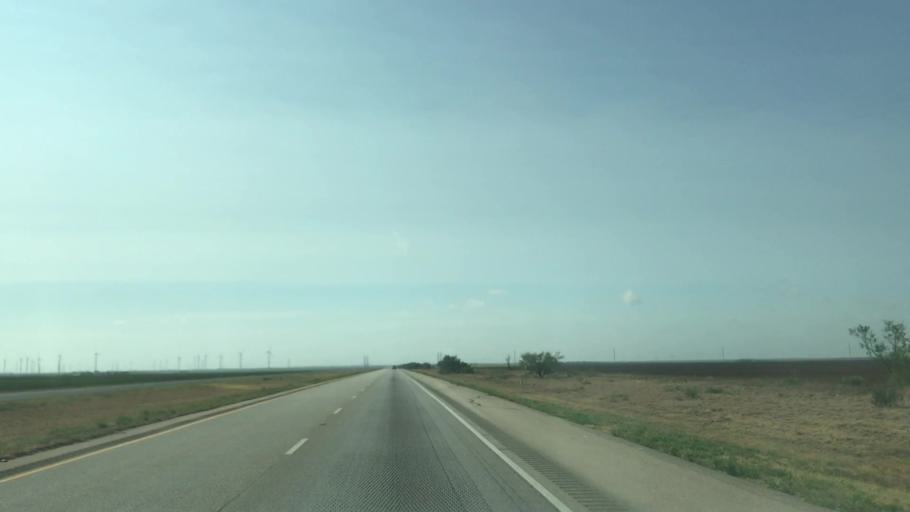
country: US
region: Texas
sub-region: Scurry County
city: Snyder
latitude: 32.6117
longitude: -100.7477
